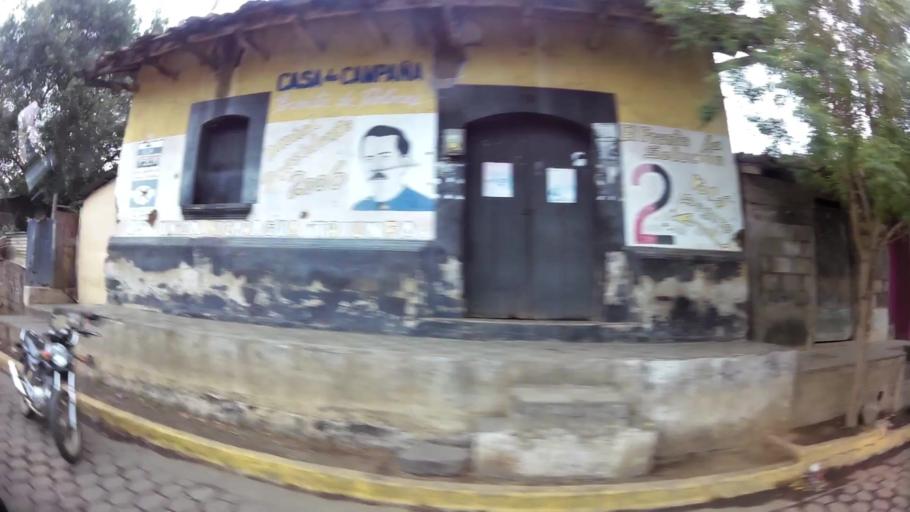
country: NI
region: Leon
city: Leon
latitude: 12.4477
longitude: -86.8766
